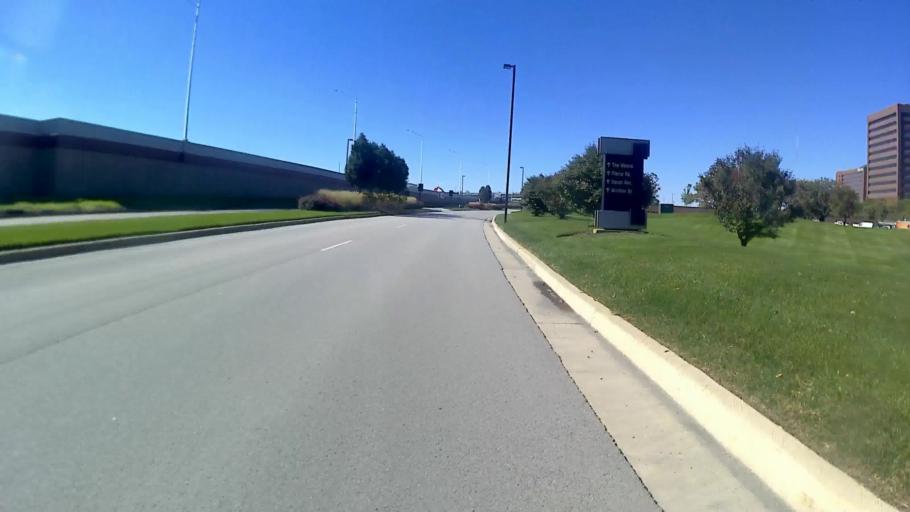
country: US
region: Illinois
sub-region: DuPage County
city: Itasca
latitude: 41.9846
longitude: -88.0154
